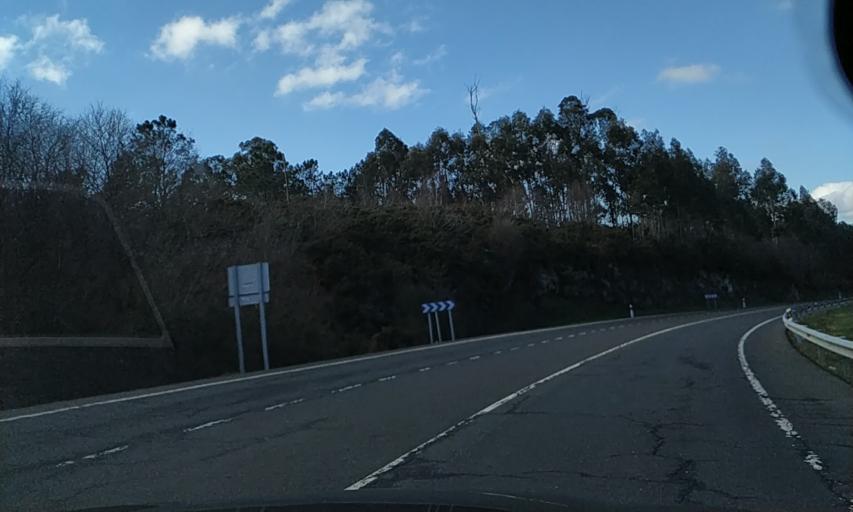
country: ES
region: Galicia
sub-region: Provincia da Coruna
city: Ribeira
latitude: 42.7114
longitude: -8.3581
